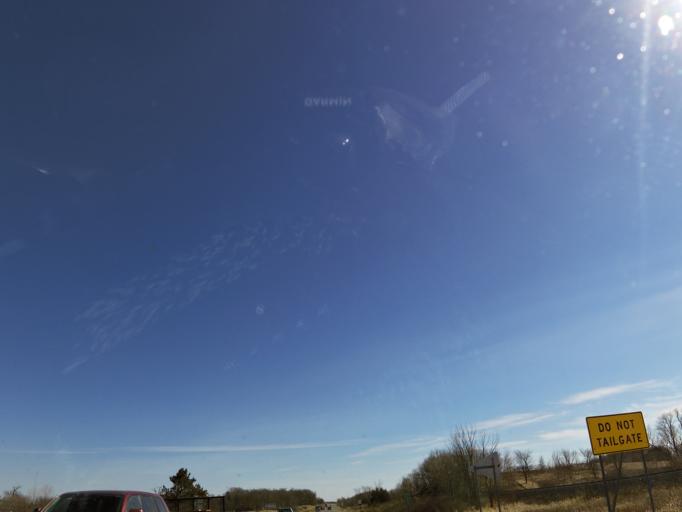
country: US
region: Minnesota
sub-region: Wright County
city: Buffalo
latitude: 45.1501
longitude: -93.8434
